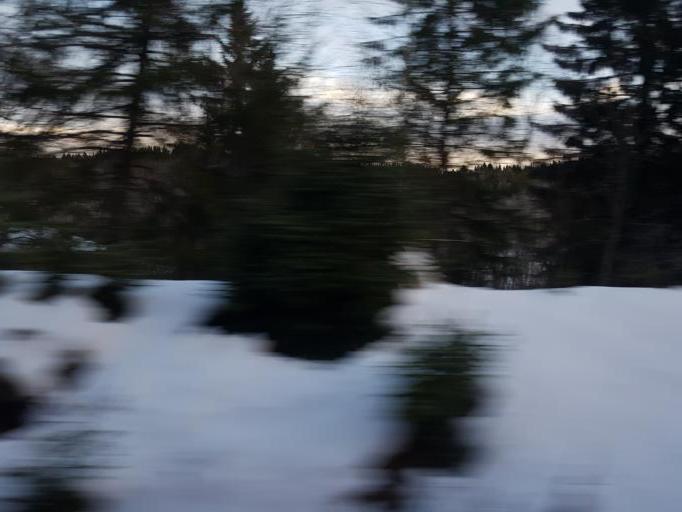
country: NO
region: Sor-Trondelag
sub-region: Rennebu
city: Berkak
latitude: 62.8699
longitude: 10.0560
